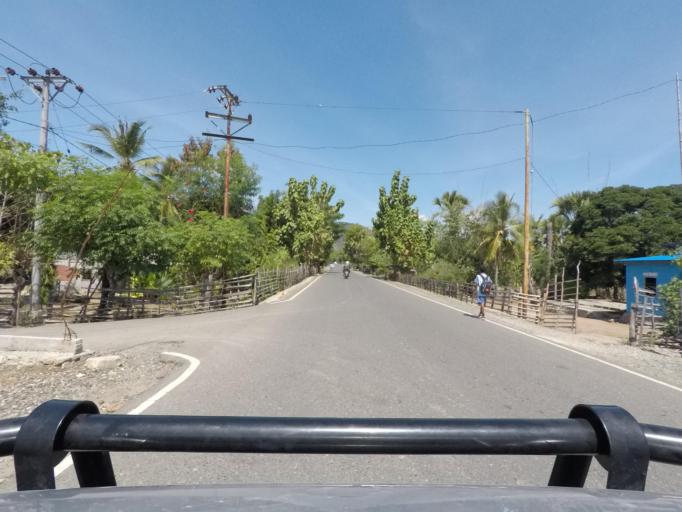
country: TL
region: Liquica
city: Maubara
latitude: -8.7863
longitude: 125.1015
